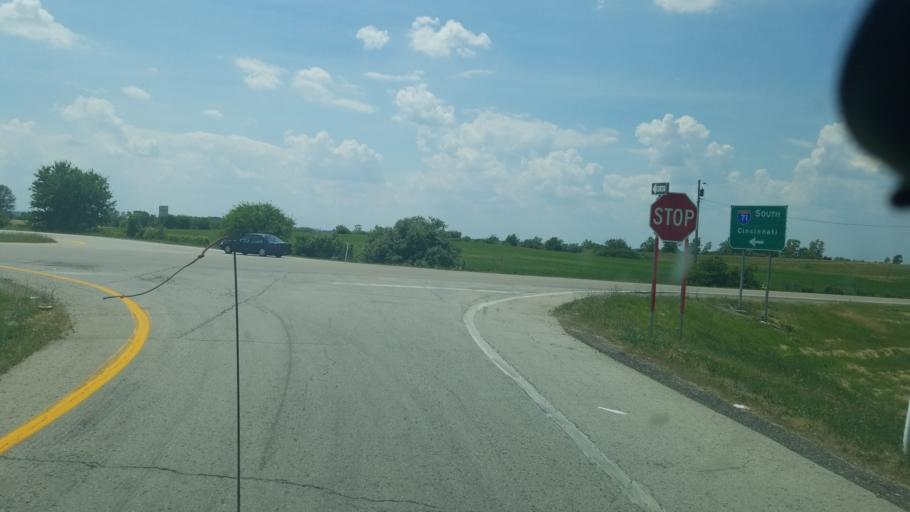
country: US
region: Ohio
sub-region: Greene County
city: Jamestown
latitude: 39.5587
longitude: -83.7196
